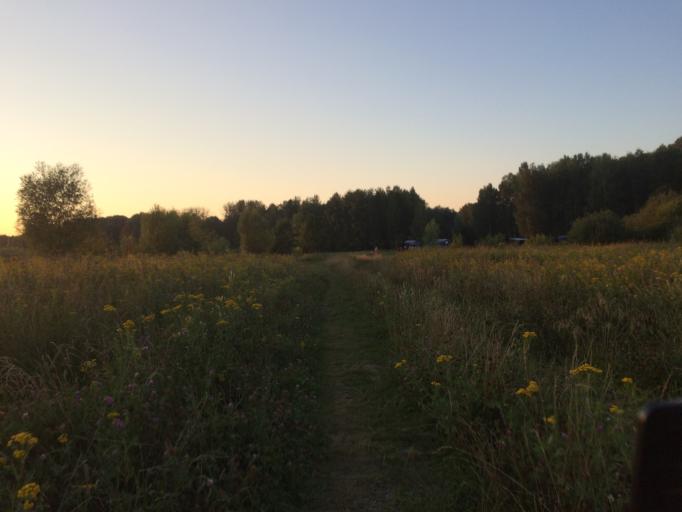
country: RU
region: Mariy-El
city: Yoshkar-Ola
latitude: 56.6207
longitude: 47.9165
